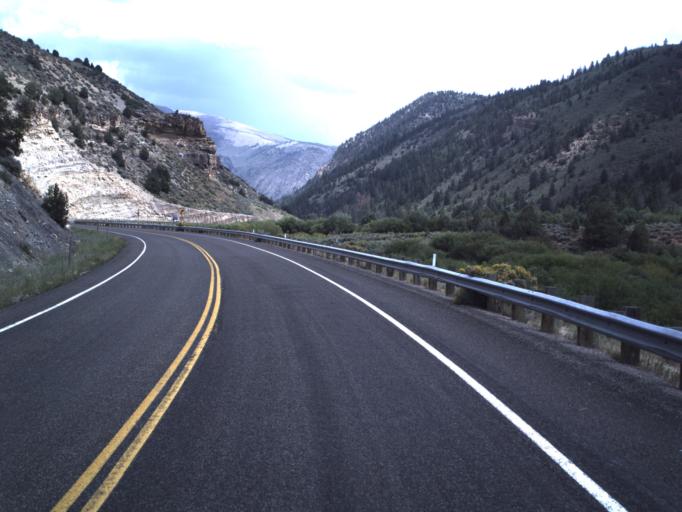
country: US
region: Utah
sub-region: Summit County
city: Francis
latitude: 40.4528
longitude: -110.8637
